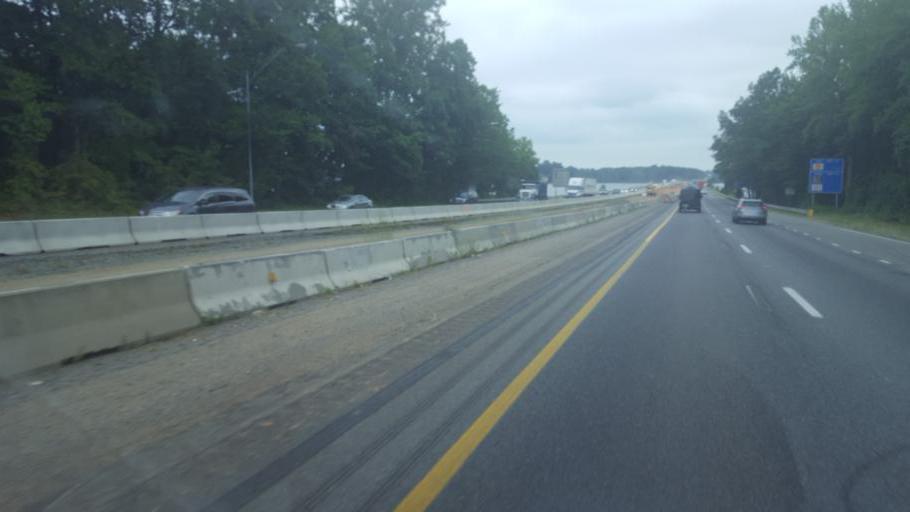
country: US
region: North Carolina
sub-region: Mecklenburg County
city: Cornelius
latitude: 35.5060
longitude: -80.8661
